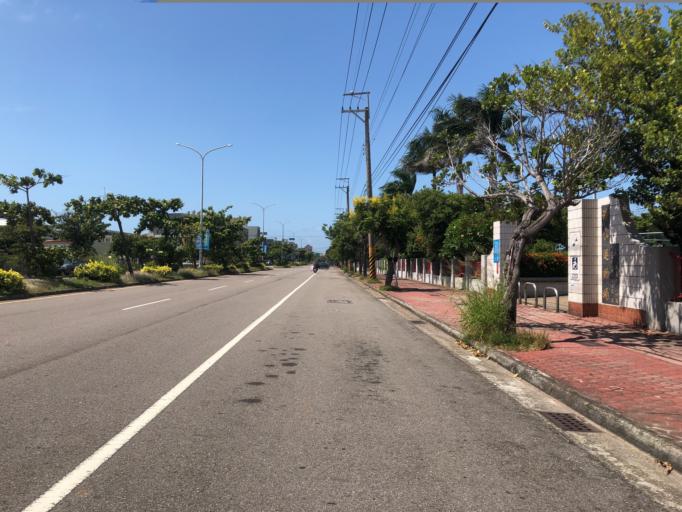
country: TW
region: Taiwan
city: Fengyuan
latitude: 24.2778
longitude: 120.5597
